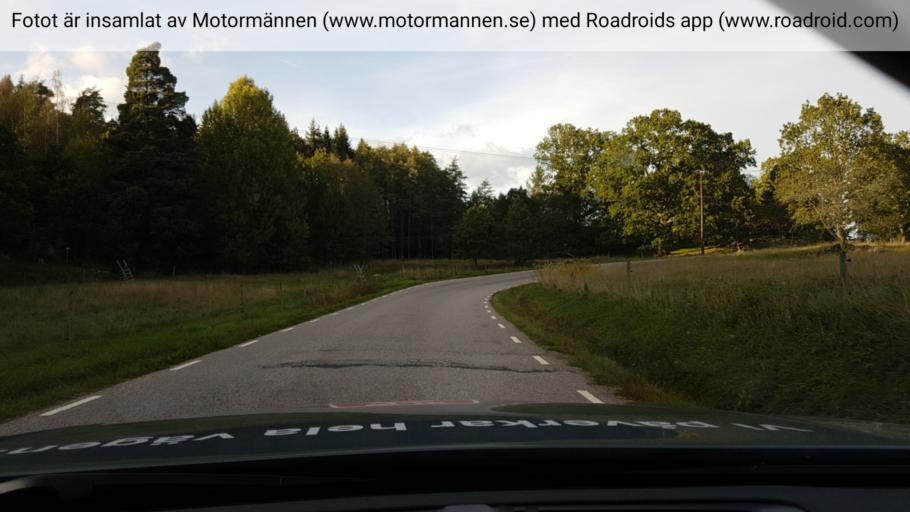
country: SE
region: Kalmar
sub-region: Vasterviks Kommun
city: Forserum
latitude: 57.9273
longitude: 16.4552
